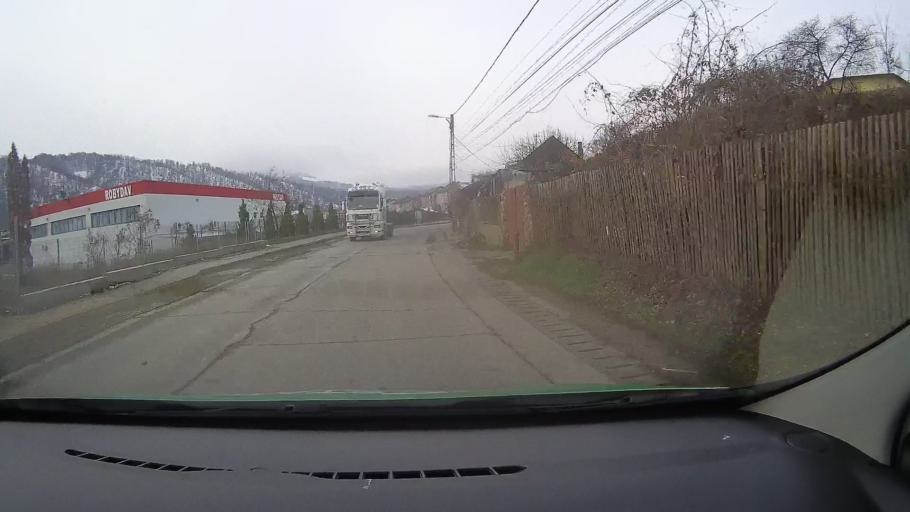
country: RO
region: Alba
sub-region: Oras Zlatna
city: Zlatna
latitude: 46.1075
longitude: 23.2333
